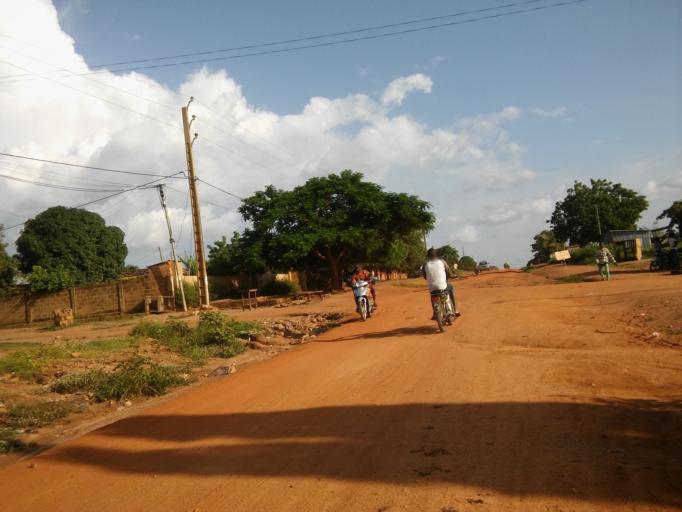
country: BJ
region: Borgou
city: Parakou
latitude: 9.3606
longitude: 2.6379
